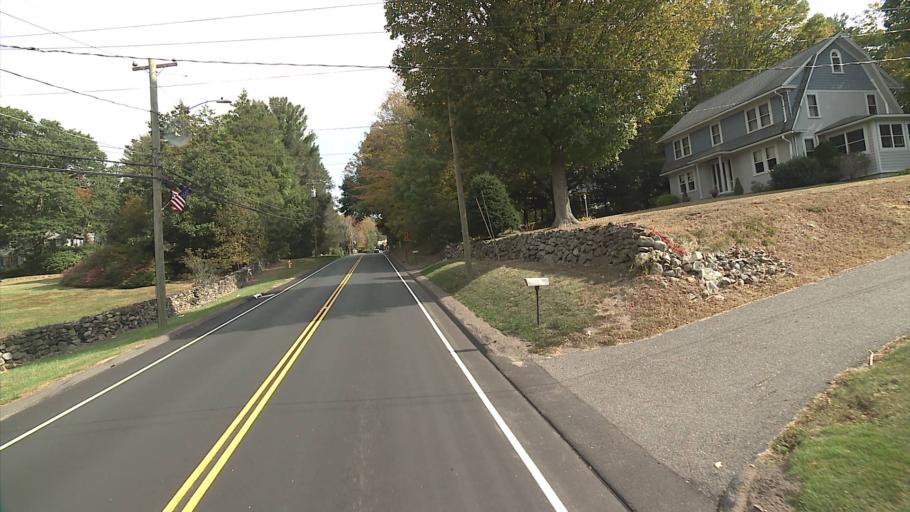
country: US
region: Connecticut
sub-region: Litchfield County
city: Watertown
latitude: 41.6107
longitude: -73.1148
